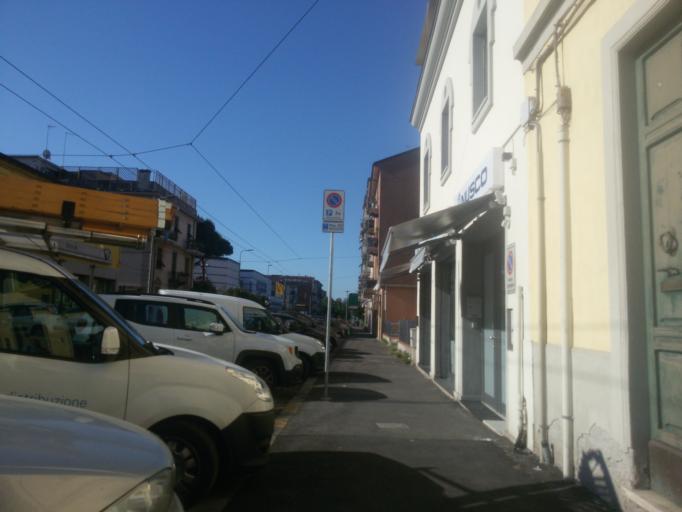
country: IT
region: Liguria
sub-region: Provincia di La Spezia
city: La Spezia
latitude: 44.1220
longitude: 9.8411
